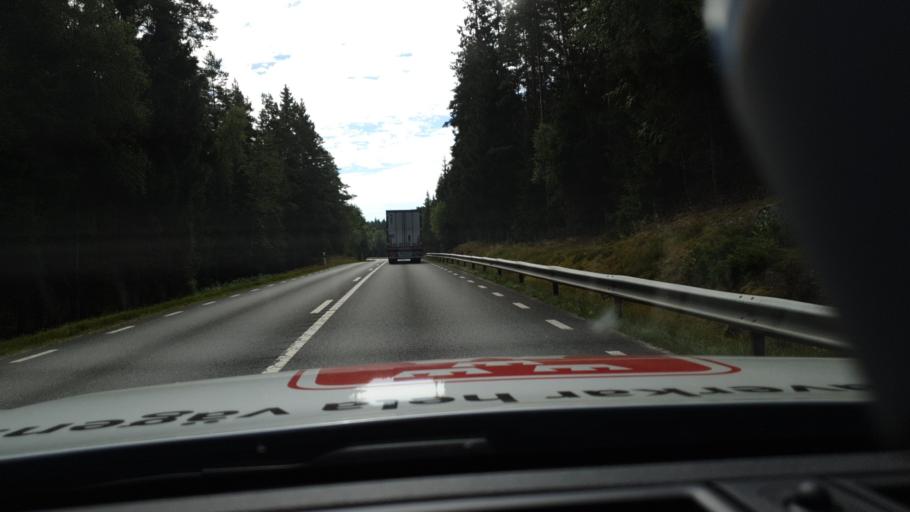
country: SE
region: Joenkoeping
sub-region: Savsjo Kommun
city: Vrigstad
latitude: 57.3801
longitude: 14.4028
